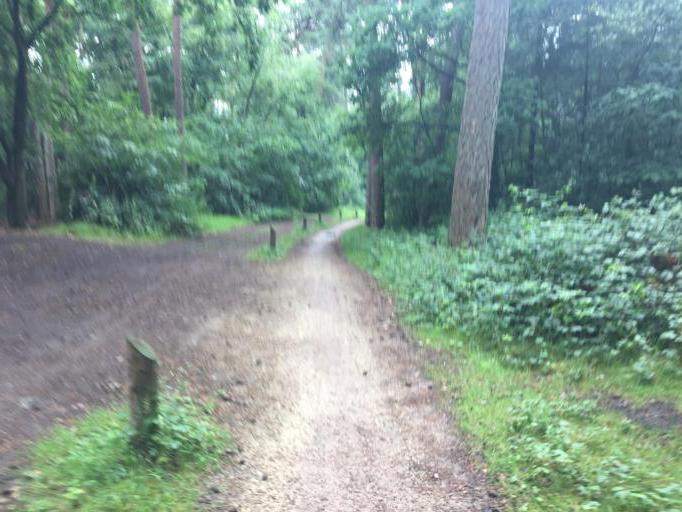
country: NL
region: Utrecht
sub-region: Gemeente Zeist
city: Zeist
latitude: 52.0826
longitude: 5.2616
